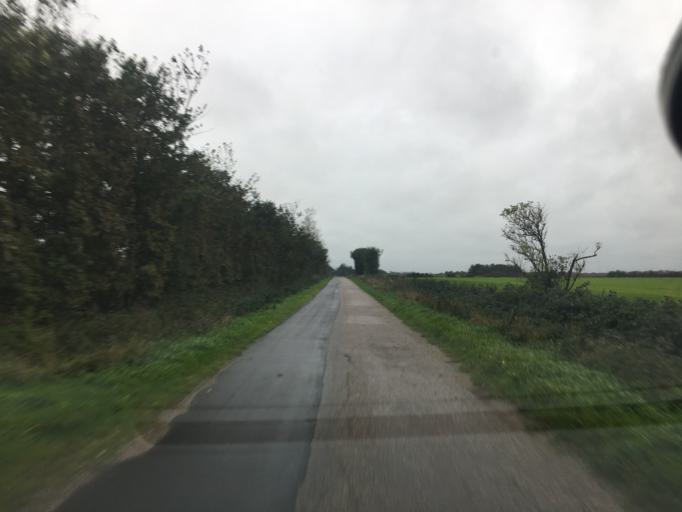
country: DE
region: Schleswig-Holstein
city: Ellhoft
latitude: 54.9457
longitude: 9.0004
